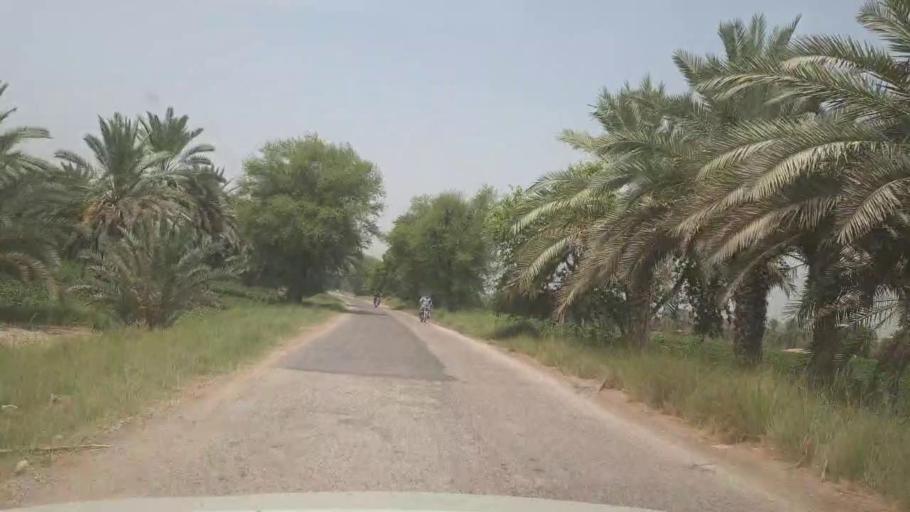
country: PK
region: Sindh
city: Kot Diji
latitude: 27.3632
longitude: 68.6943
